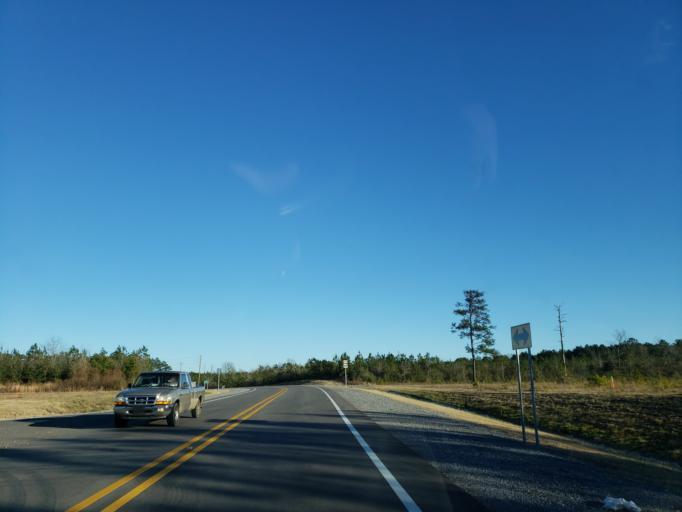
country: US
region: Mississippi
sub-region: Forrest County
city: Rawls Springs
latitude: 31.4190
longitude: -89.4135
